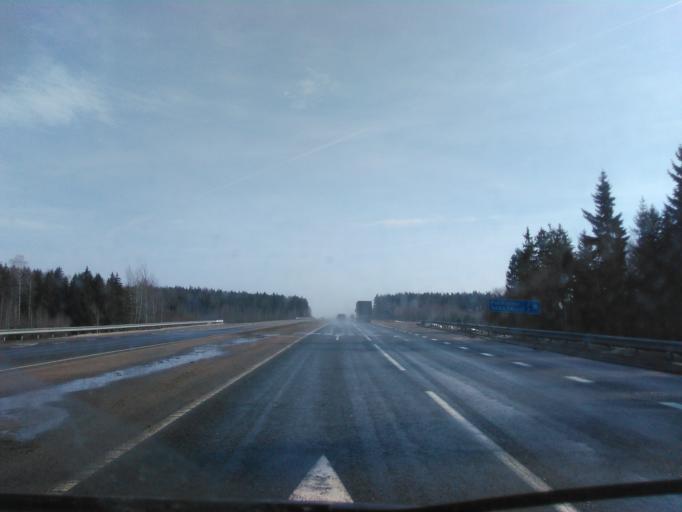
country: BY
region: Vitebsk
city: Kokhanava
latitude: 54.4780
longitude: 29.8468
